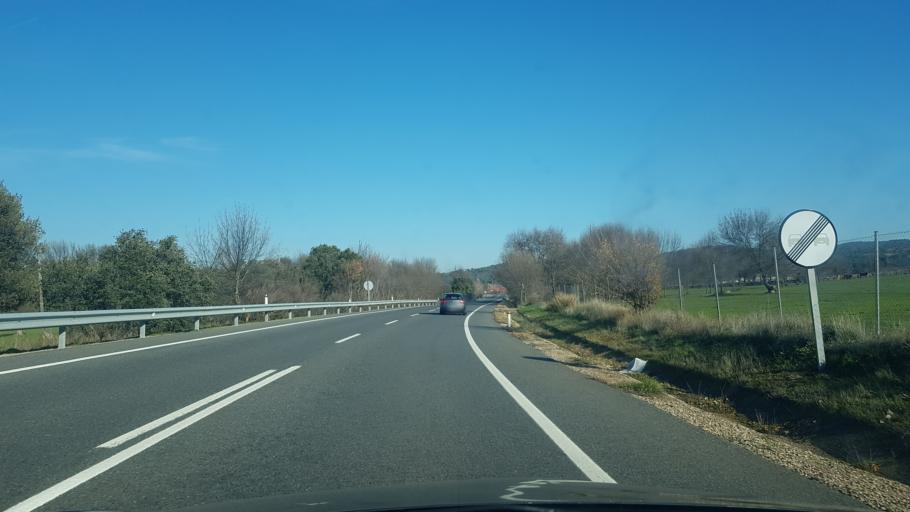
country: ES
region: Madrid
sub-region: Provincia de Madrid
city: Rozas de Puerto Real
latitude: 40.3431
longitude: -4.4542
